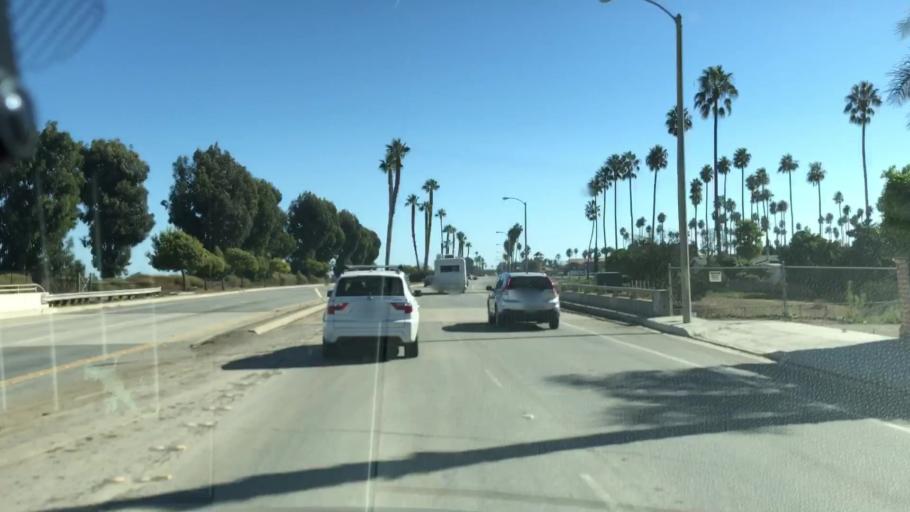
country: US
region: California
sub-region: Ventura County
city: Ventura
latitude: 34.2530
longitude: -119.2591
